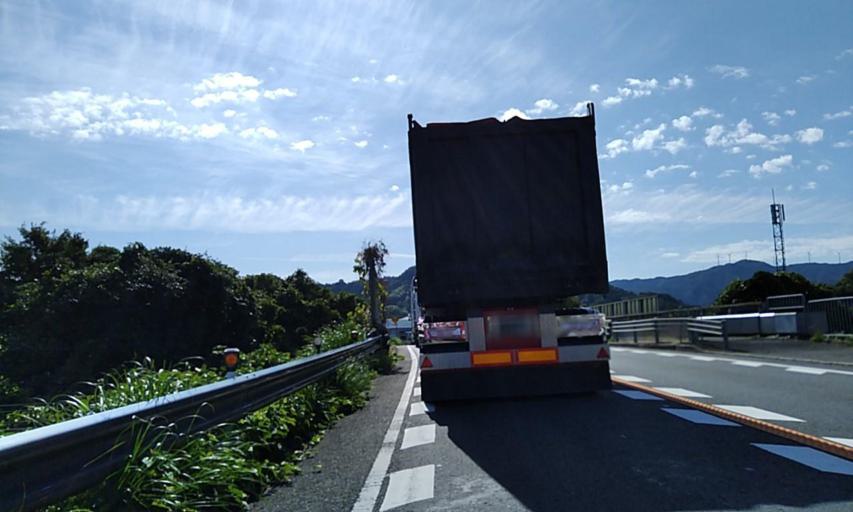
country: JP
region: Wakayama
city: Kainan
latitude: 34.0368
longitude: 135.1851
